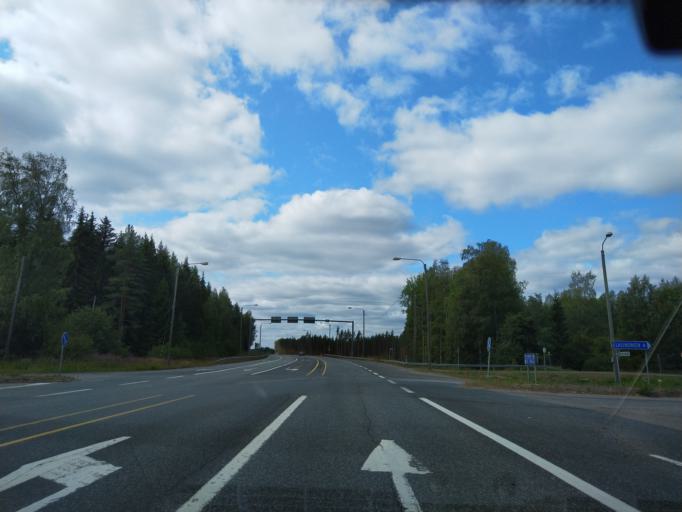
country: FI
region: Haeme
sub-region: Haemeenlinna
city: Tervakoski
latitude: 60.7446
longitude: 24.6483
